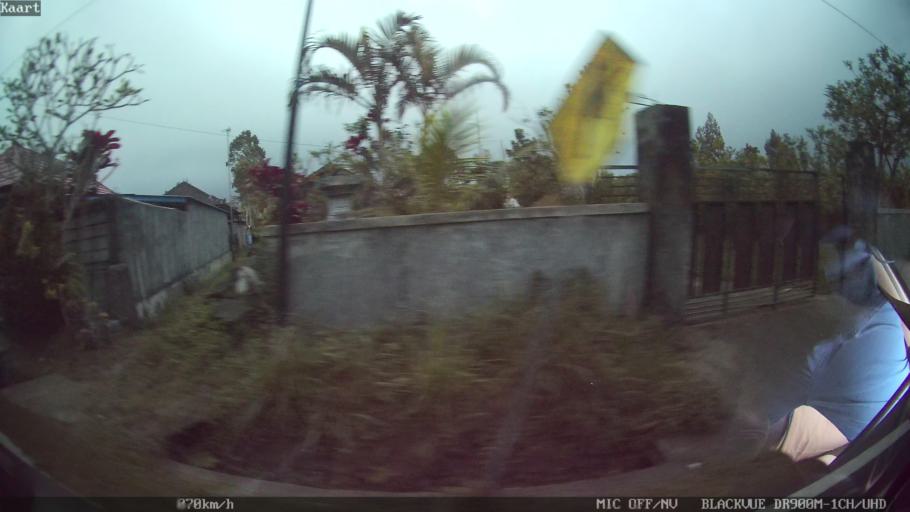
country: ID
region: Bali
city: Banjar Kedisan
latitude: -8.2753
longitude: 115.3285
